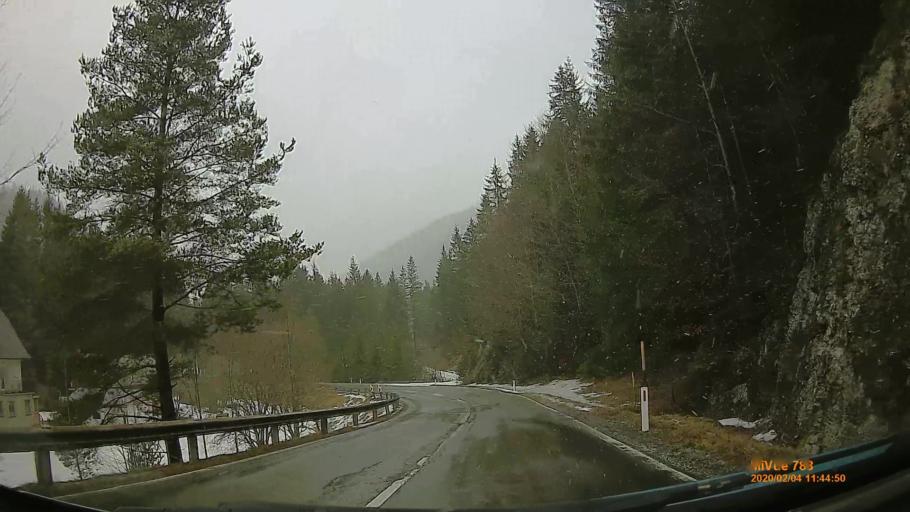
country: AT
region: Styria
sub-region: Politischer Bezirk Bruck-Muerzzuschlag
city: Muerzsteg
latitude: 47.6896
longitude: 15.4794
